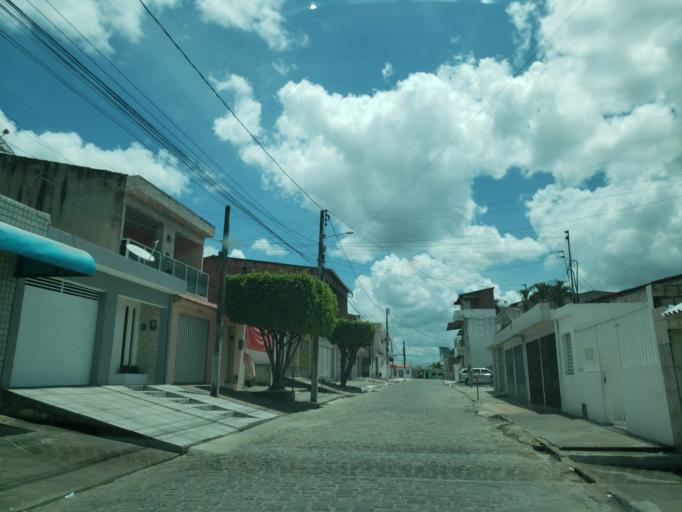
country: BR
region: Alagoas
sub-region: Uniao Dos Palmares
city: Uniao dos Palmares
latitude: -9.1644
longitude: -36.0224
